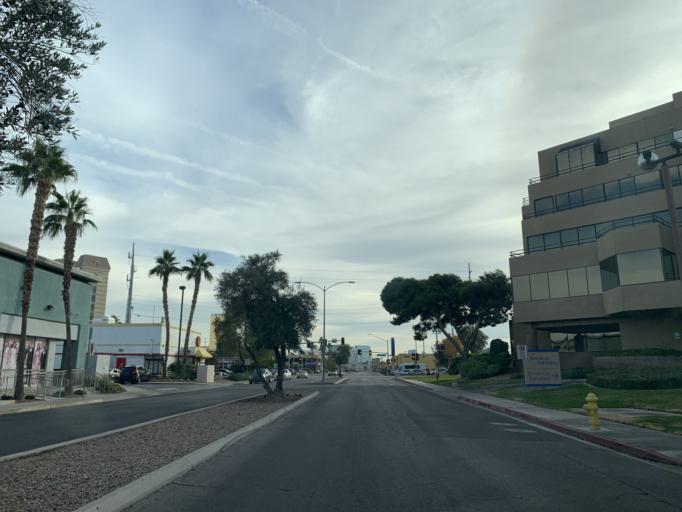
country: US
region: Nevada
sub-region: Clark County
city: Las Vegas
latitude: 36.1454
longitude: -115.1776
